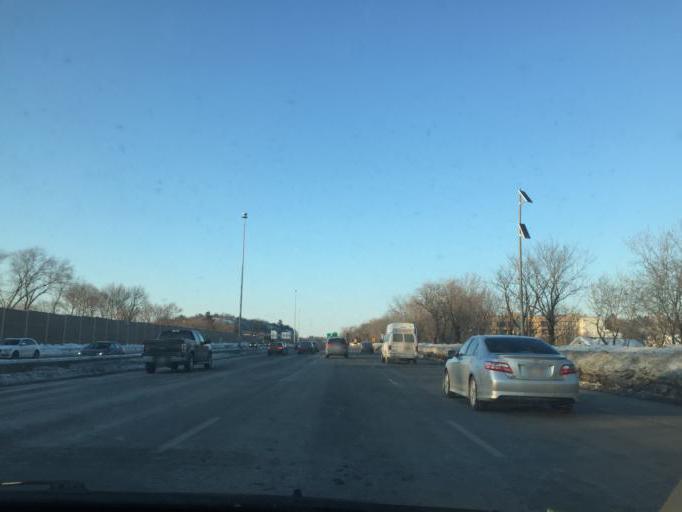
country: US
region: Massachusetts
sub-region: Middlesex County
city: Medford
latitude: 42.4234
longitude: -71.1033
